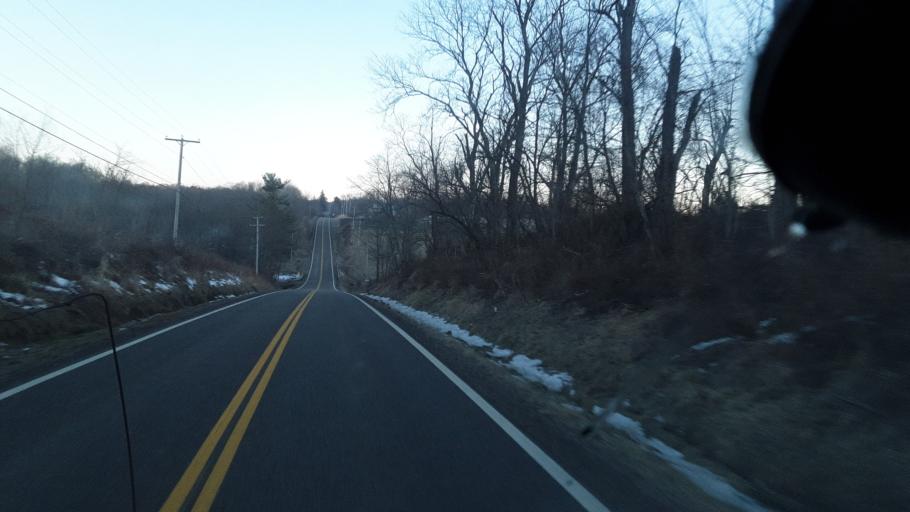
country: US
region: Ohio
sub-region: Perry County
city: Somerset
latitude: 39.7917
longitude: -82.3010
